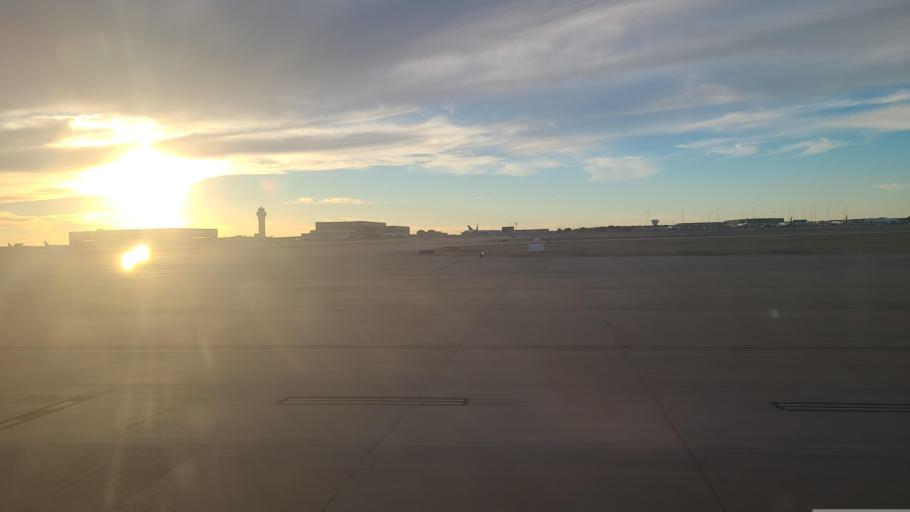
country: US
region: Texas
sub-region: Tarrant County
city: Grapevine
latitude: 32.9106
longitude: -97.0479
